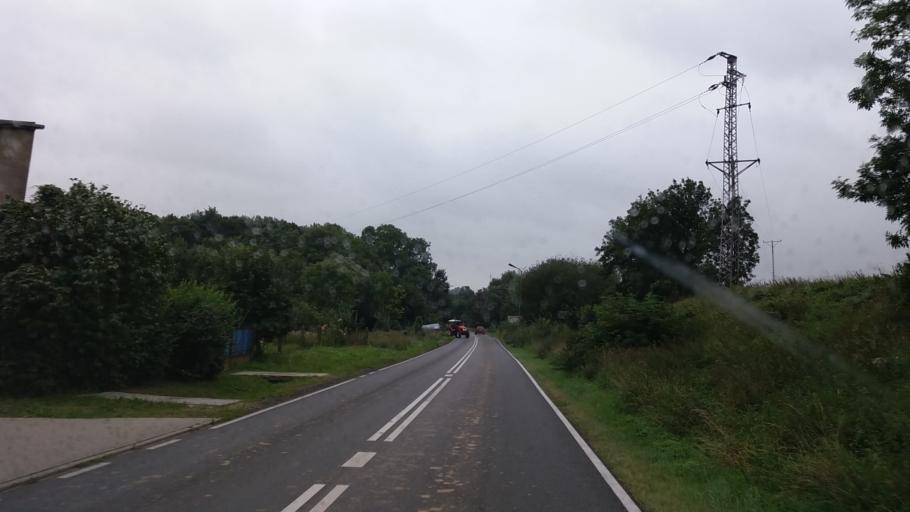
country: PL
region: West Pomeranian Voivodeship
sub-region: Powiat choszczenski
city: Pelczyce
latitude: 53.0508
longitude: 15.2989
